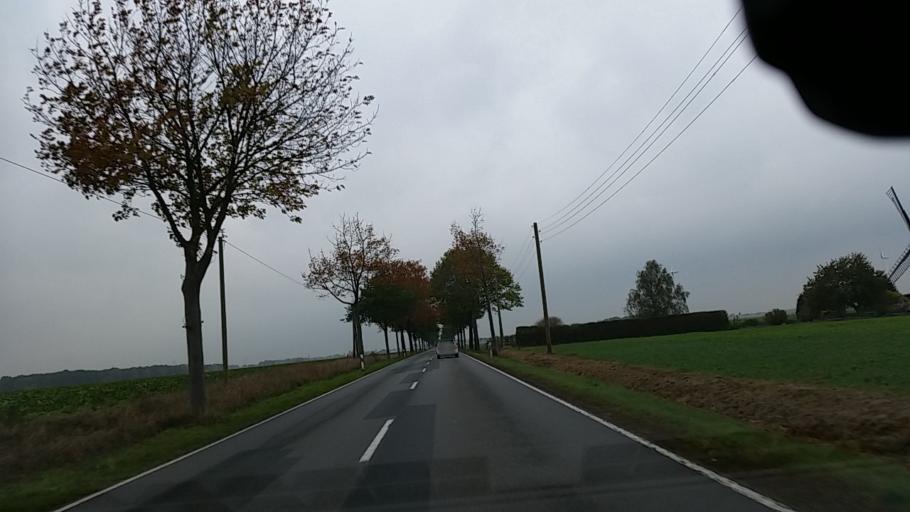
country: DE
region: Lower Saxony
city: Wittingen
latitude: 52.6999
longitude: 10.8025
